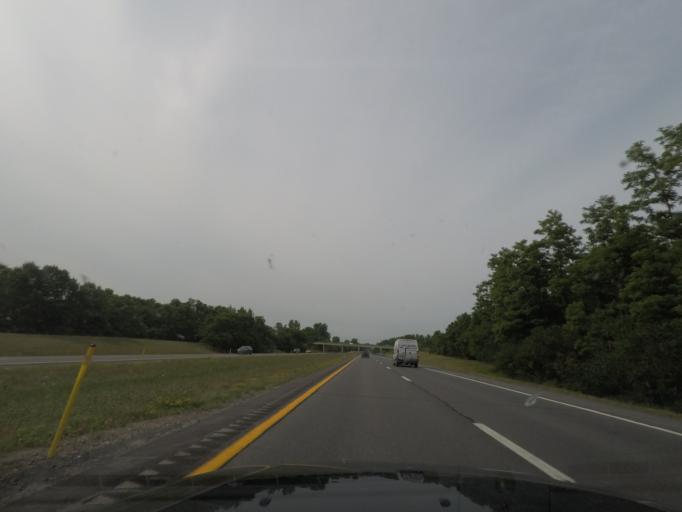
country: US
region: New York
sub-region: Clinton County
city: Plattsburgh West
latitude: 44.6326
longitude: -73.4833
